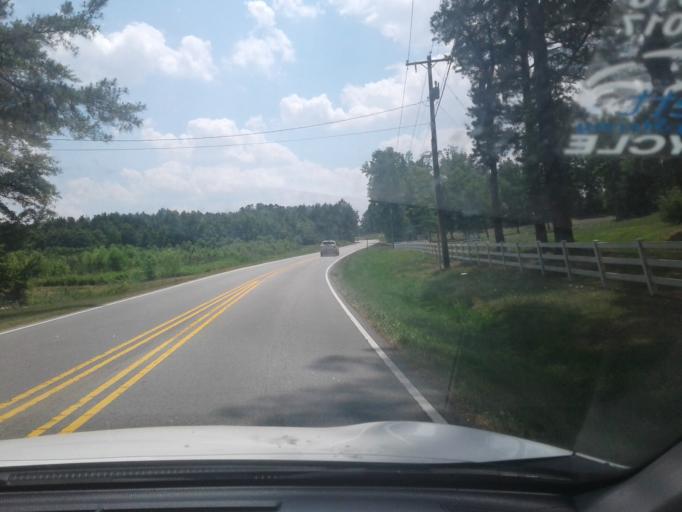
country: US
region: North Carolina
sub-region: Johnston County
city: Benson
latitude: 35.4012
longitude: -78.5417
